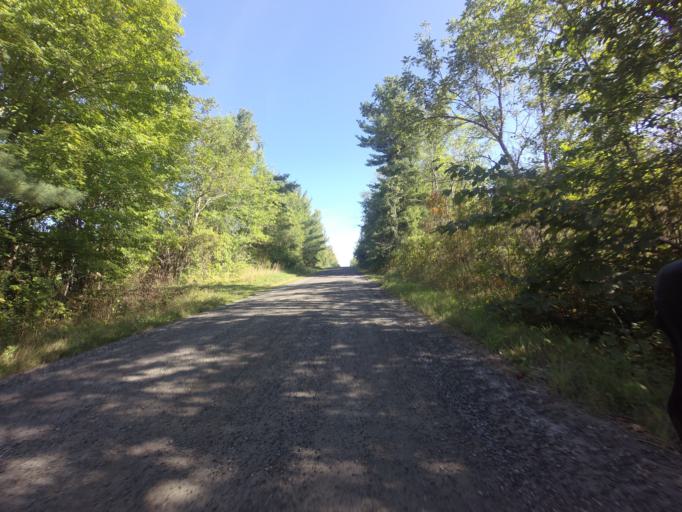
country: CA
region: Ontario
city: Perth
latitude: 44.9320
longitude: -76.3715
